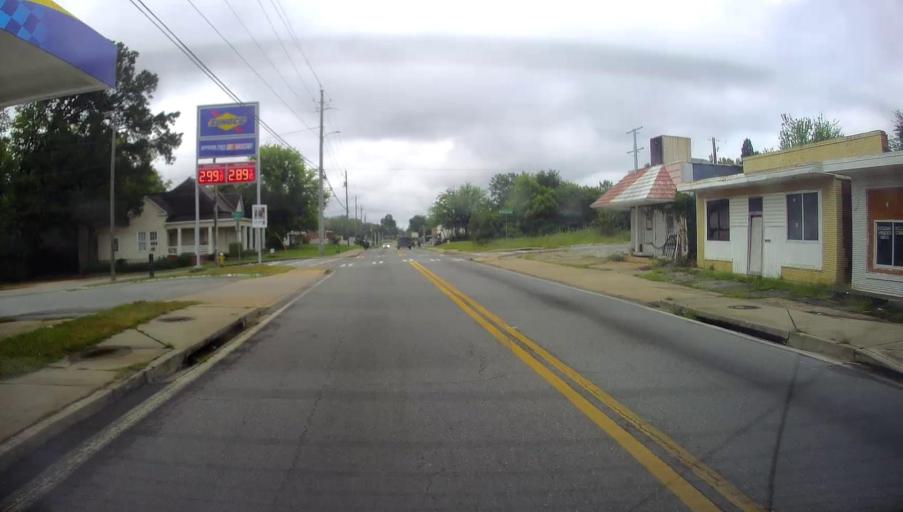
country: US
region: Georgia
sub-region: Bibb County
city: Macon
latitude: 32.7946
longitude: -83.6543
